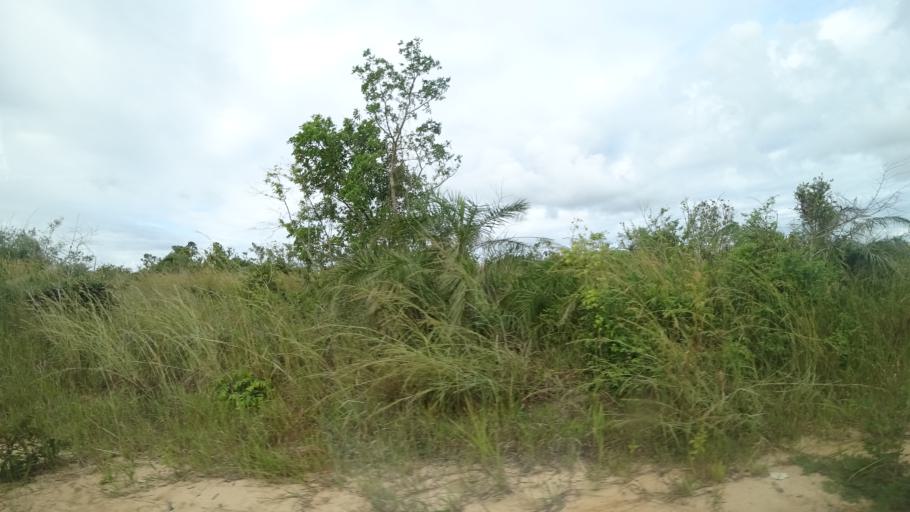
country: MZ
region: Sofala
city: Beira
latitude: -19.6192
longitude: 35.0605
